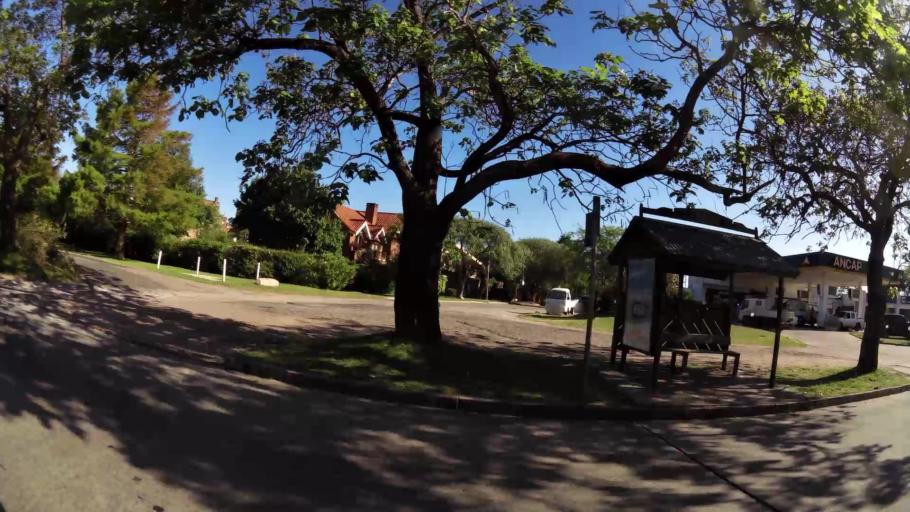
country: UY
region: Canelones
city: Paso de Carrasco
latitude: -34.8777
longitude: -56.0623
